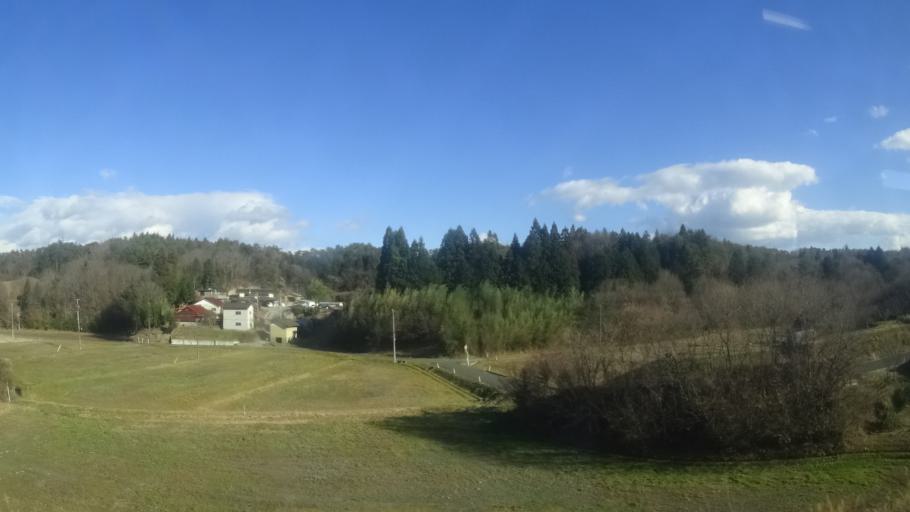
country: JP
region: Fukushima
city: Namie
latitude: 37.6735
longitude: 140.9718
